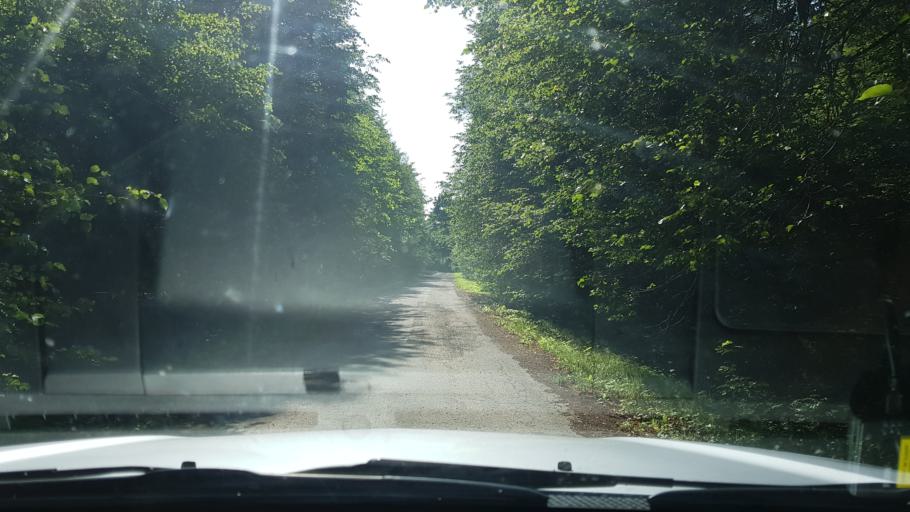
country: EE
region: Ida-Virumaa
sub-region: Sillamaee linn
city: Sillamae
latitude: 59.3482
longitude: 27.7365
